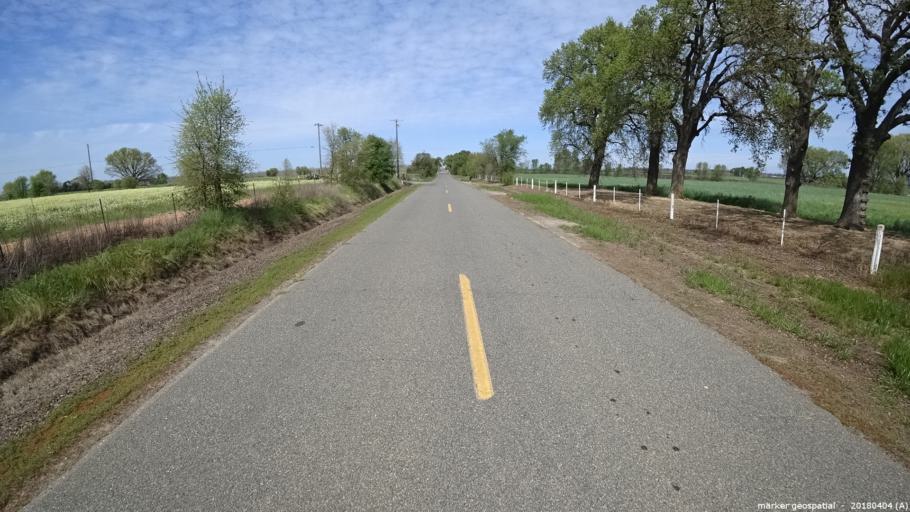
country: US
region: California
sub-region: Sacramento County
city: Herald
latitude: 38.2734
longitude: -121.2082
